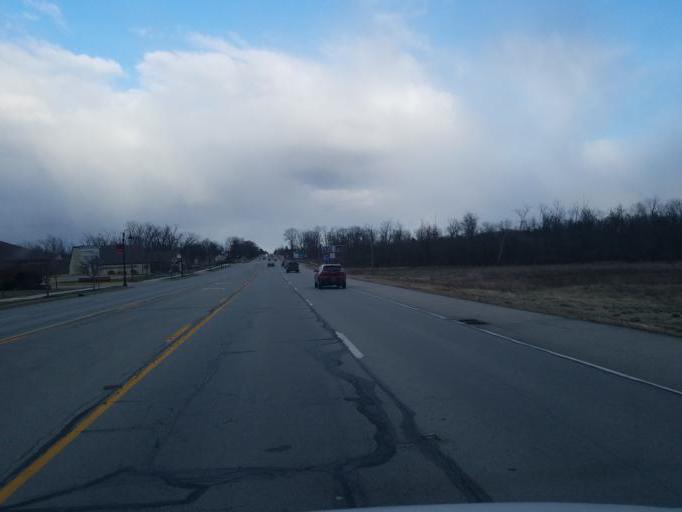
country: US
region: Indiana
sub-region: Marion County
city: Cumberland
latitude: 39.7767
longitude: -85.9512
